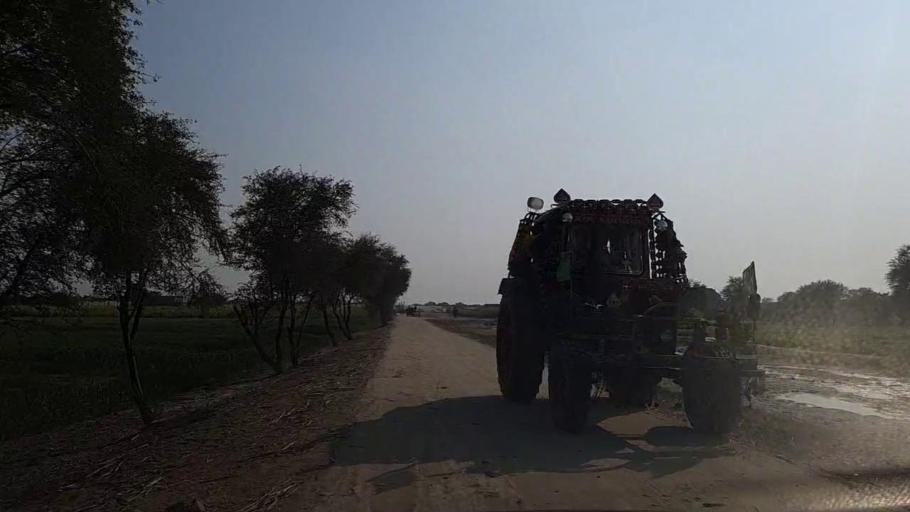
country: PK
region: Sindh
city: Daur
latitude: 26.4007
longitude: 68.4174
